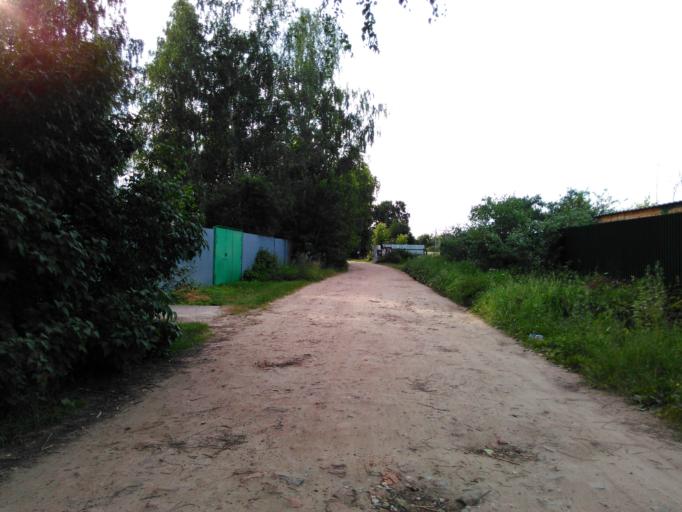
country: RU
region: Moskovskaya
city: Vishnyakovskiye Dachi
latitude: 55.7675
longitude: 38.1518
